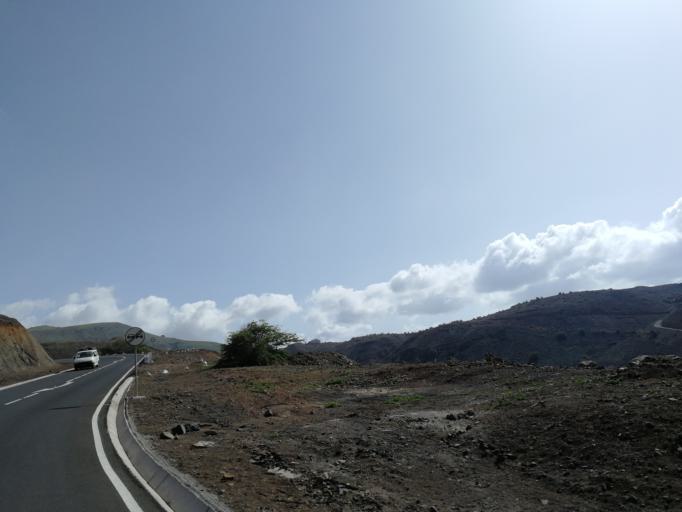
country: CV
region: Sao Vicente
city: Mindelo
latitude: 16.8835
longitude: -24.9399
